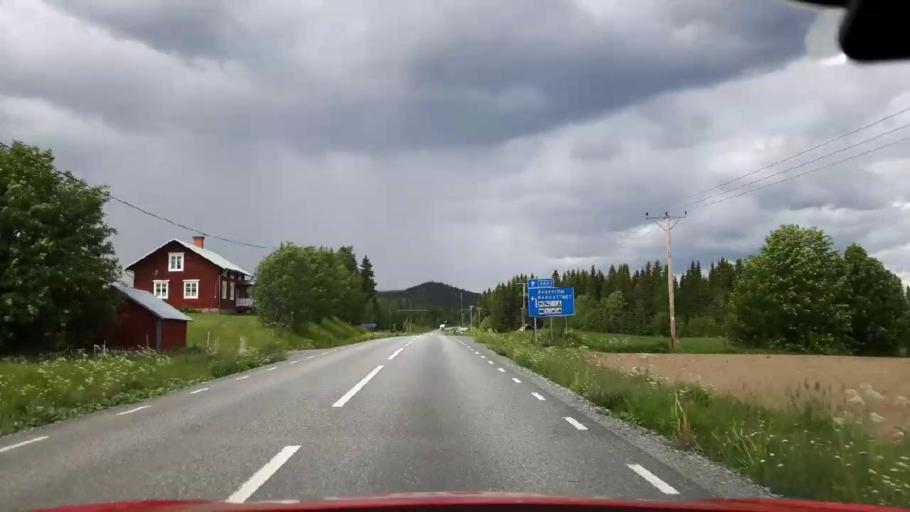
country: SE
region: Jaemtland
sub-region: Krokoms Kommun
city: Krokom
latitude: 63.6812
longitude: 14.3331
